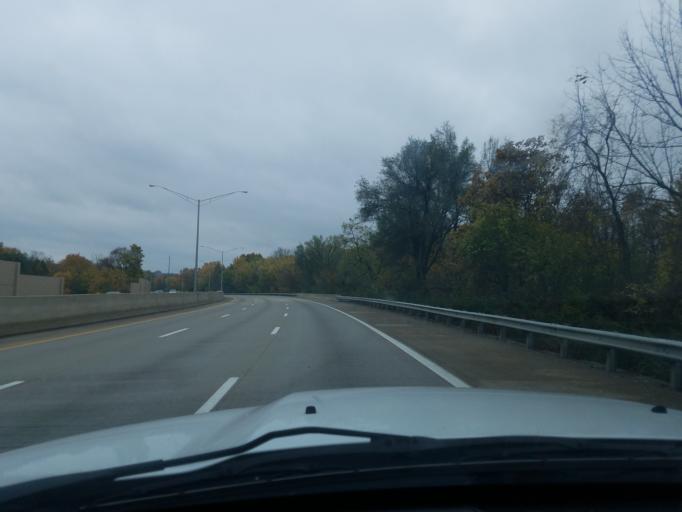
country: US
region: Kentucky
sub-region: Jefferson County
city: Shively
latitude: 38.1912
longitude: -85.8306
